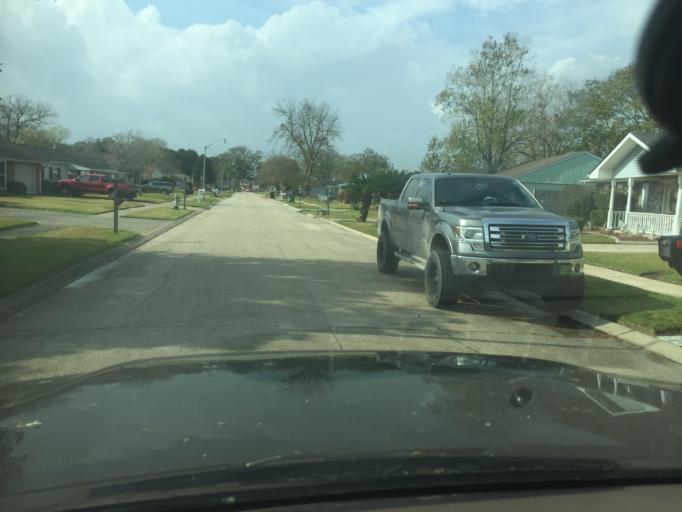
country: US
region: Louisiana
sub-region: Jefferson Parish
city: Avondale
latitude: 29.9152
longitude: -90.2021
